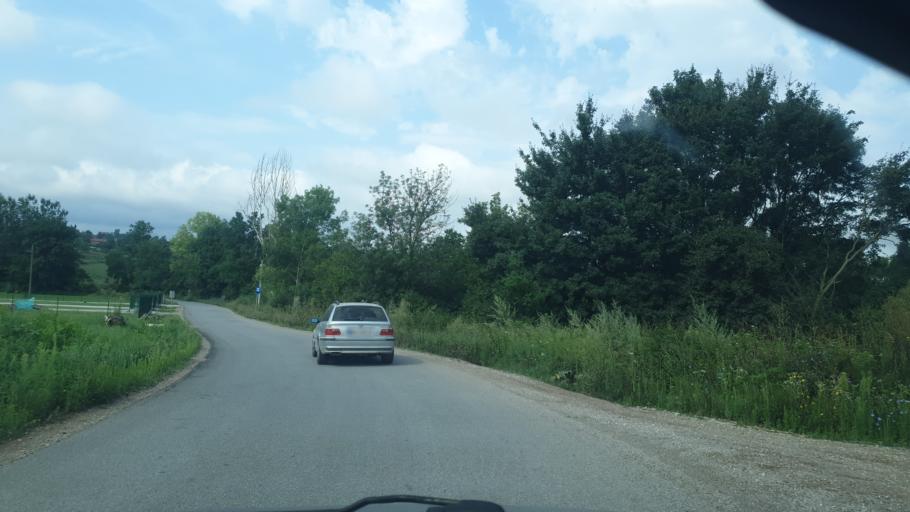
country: RS
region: Central Serbia
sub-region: Sumadijski Okrug
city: Kragujevac
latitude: 44.1112
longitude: 20.8309
